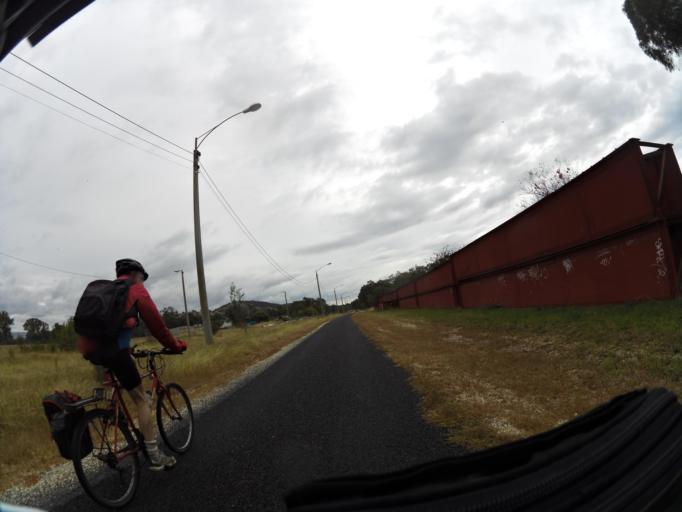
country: AU
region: Victoria
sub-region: Wodonga
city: Wodonga
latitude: -36.1495
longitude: 146.9387
